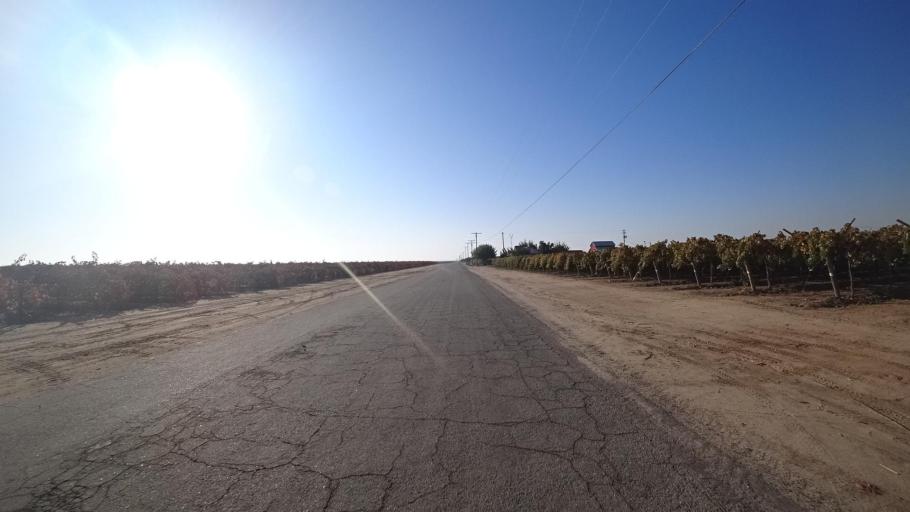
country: US
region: California
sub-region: Tulare County
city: Richgrove
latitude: 35.7714
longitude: -119.1518
